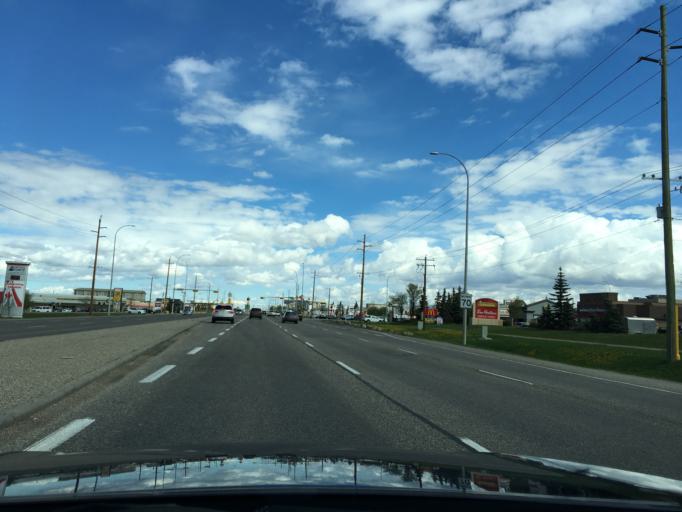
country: CA
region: Alberta
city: Calgary
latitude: 51.0719
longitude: -114.0016
